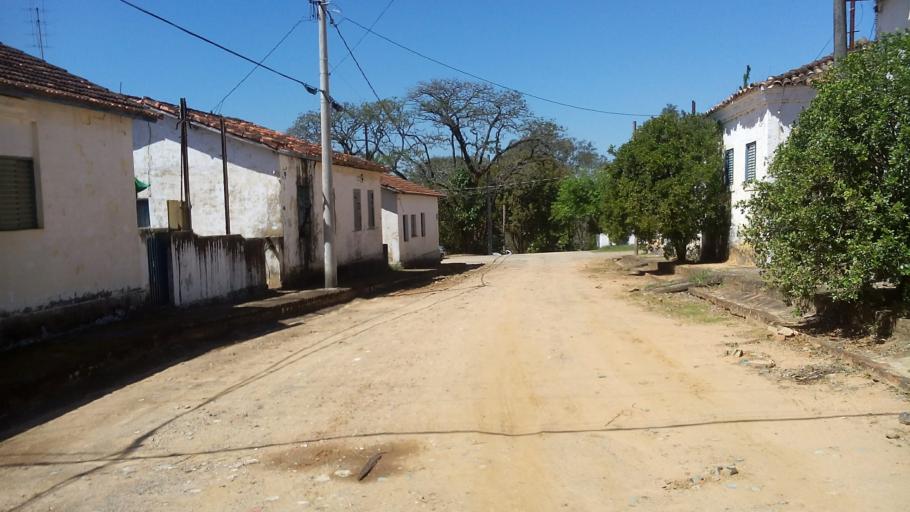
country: BR
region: Sao Paulo
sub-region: Aracoiaba Da Serra
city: Aracoiaba da Serra
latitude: -23.4263
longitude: -47.5989
